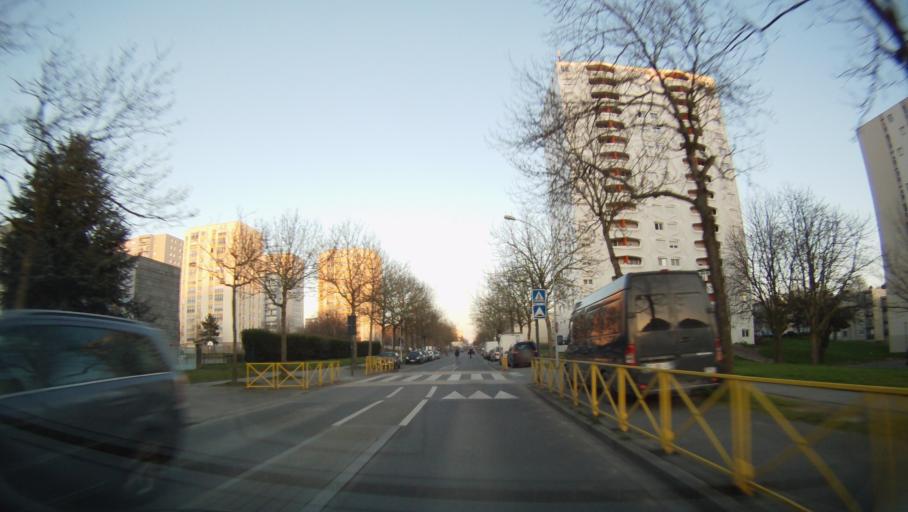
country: FR
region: Brittany
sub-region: Departement d'Ille-et-Vilaine
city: Rennes
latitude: 48.0865
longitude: -1.6642
